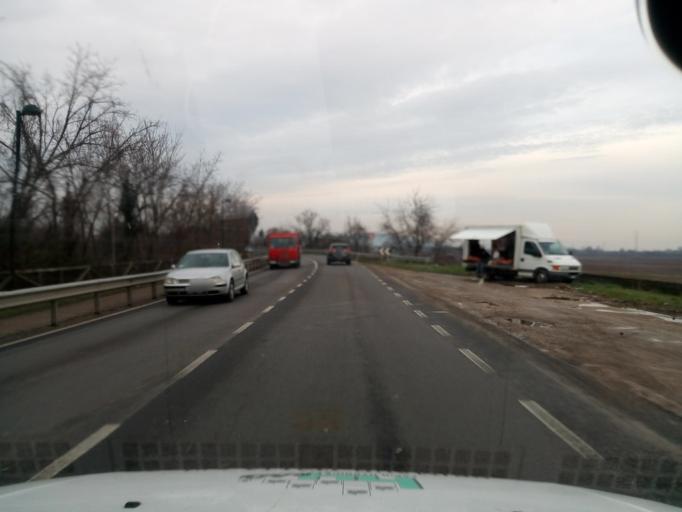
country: IT
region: Veneto
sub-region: Provincia di Vicenza
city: Montebello Vicentino
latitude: 45.4586
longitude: 11.3897
